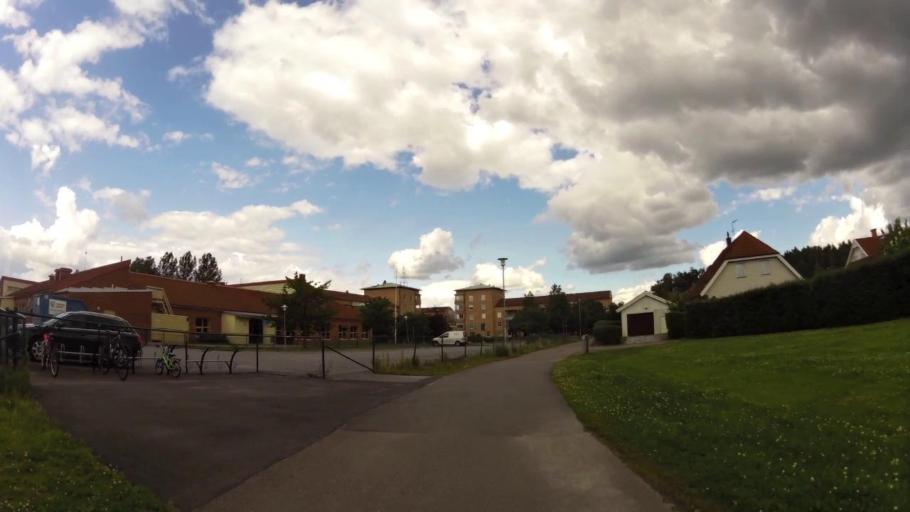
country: SE
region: OEstergoetland
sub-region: Linkopings Kommun
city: Ekangen
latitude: 58.4317
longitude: 15.6925
